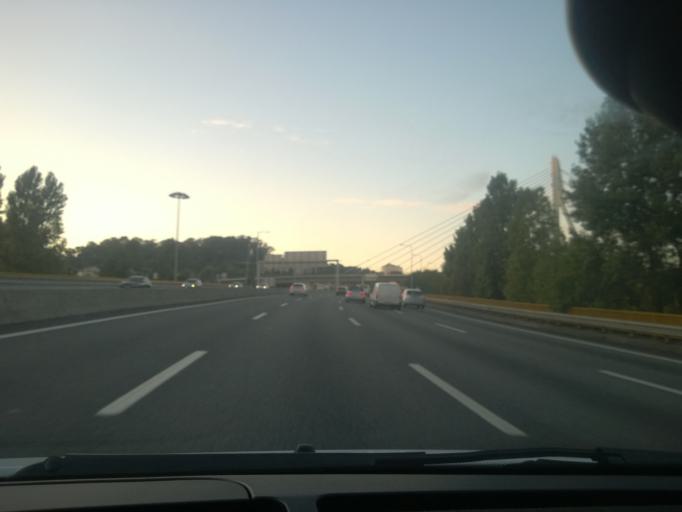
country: PT
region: Porto
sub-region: Gondomar
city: Valbom
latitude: 41.1539
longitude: -8.5822
